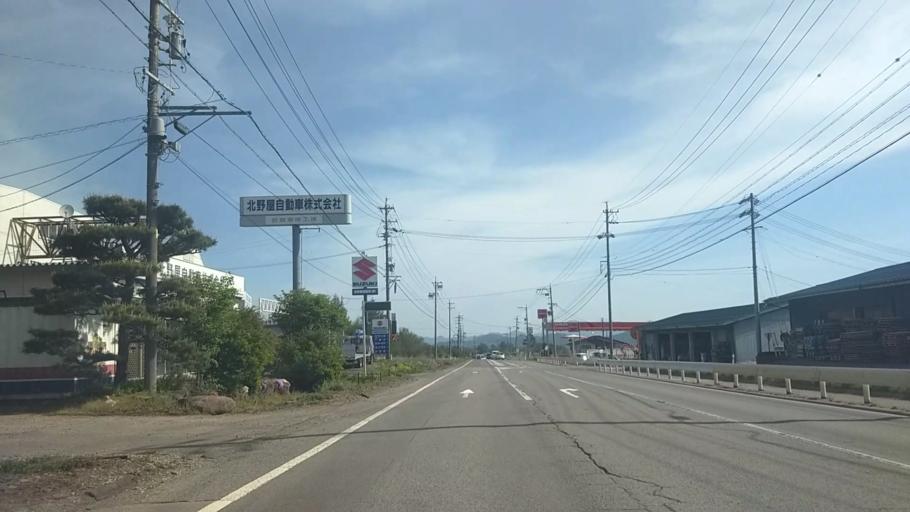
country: JP
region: Nagano
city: Saku
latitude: 35.9828
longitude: 138.4847
